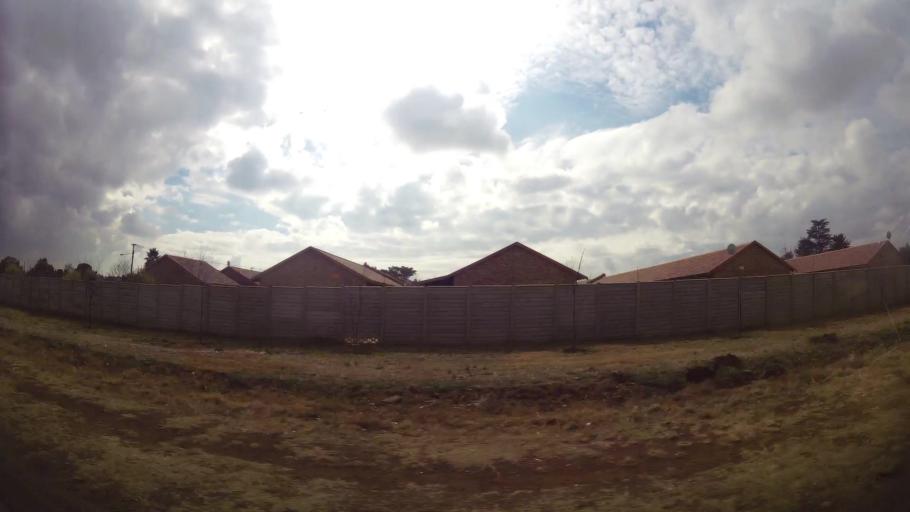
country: ZA
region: Gauteng
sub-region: Sedibeng District Municipality
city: Meyerton
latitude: -26.5977
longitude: 28.0336
